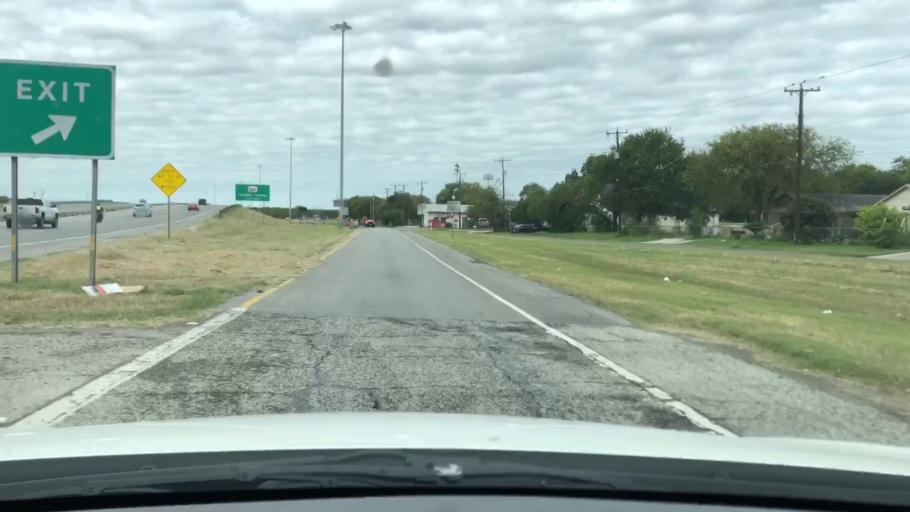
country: US
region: Texas
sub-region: Bexar County
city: Lackland Air Force Base
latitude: 29.4077
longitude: -98.5967
